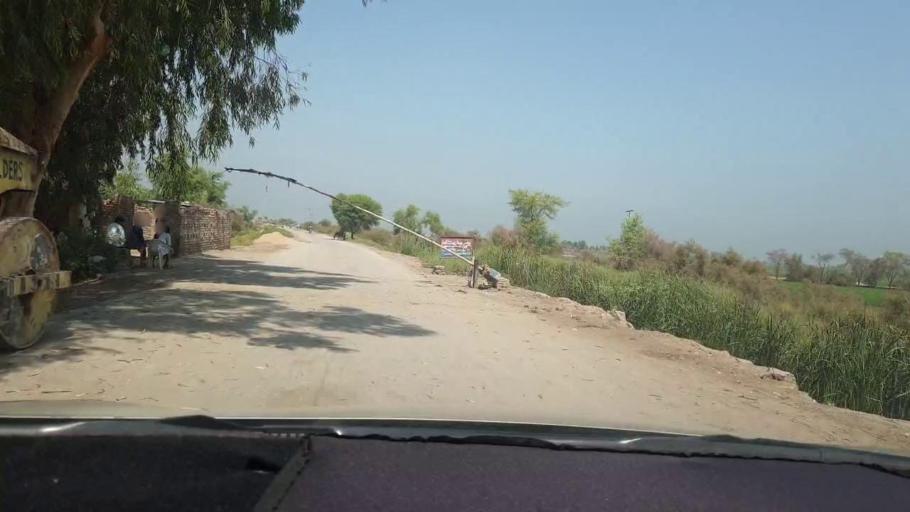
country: PK
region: Sindh
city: Miro Khan
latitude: 27.8211
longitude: 68.0229
